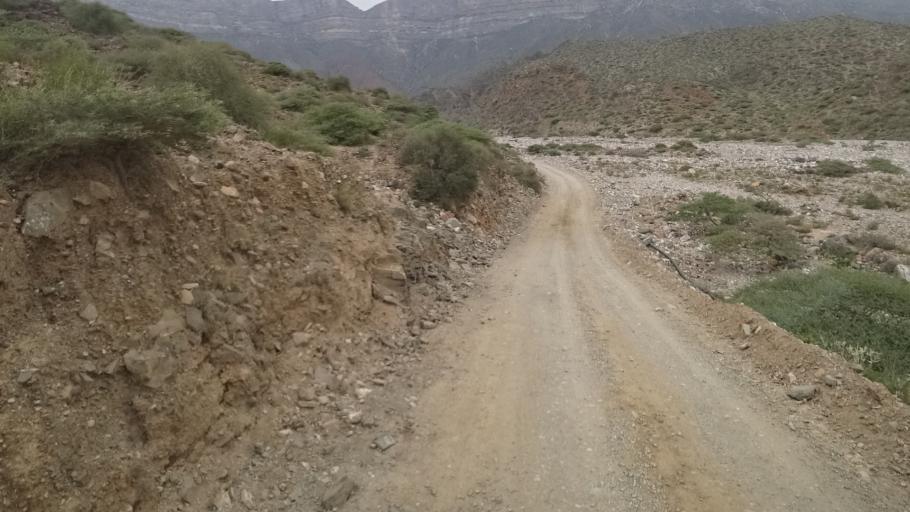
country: OM
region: Zufar
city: Salalah
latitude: 17.1756
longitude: 54.9502
